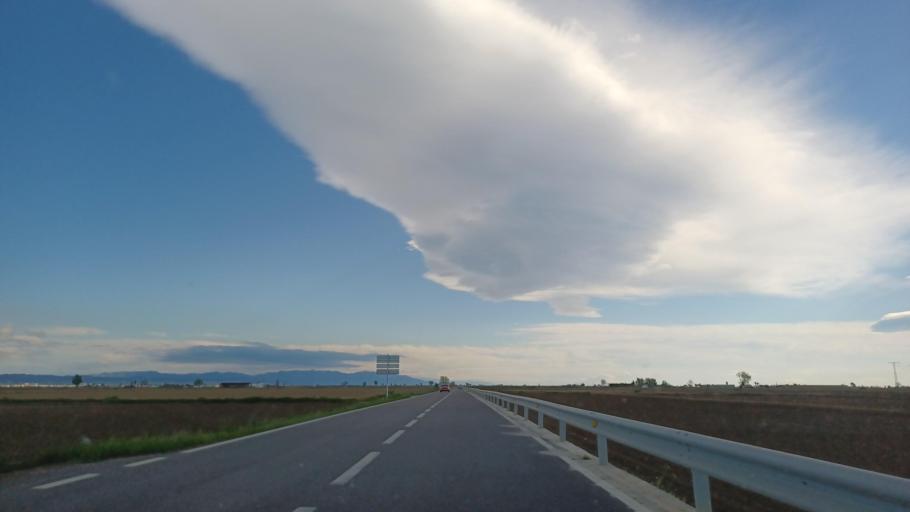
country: ES
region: Catalonia
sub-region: Provincia de Tarragona
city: Deltebre
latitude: 40.7325
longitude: 0.7105
